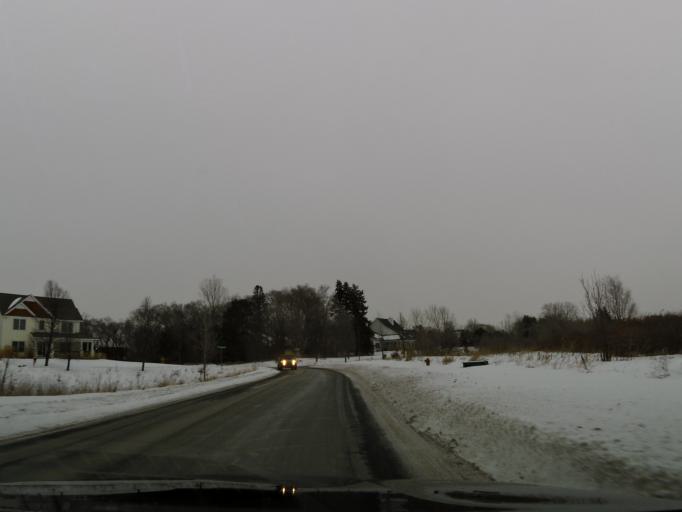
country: US
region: Minnesota
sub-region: Washington County
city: Lake Elmo
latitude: 45.0091
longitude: -92.8688
